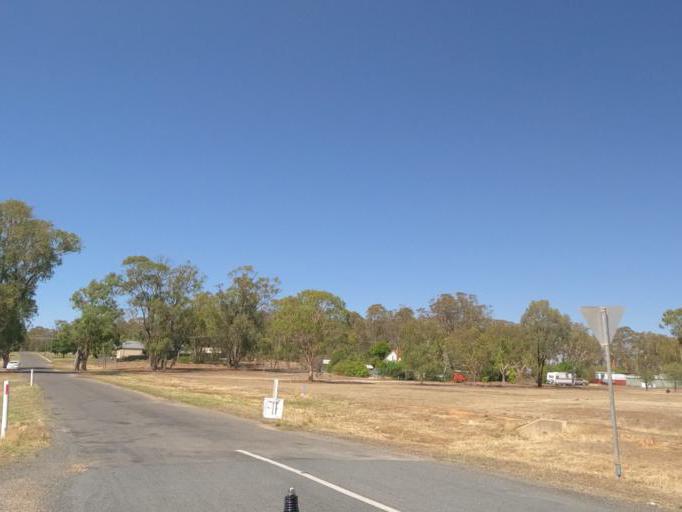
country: AU
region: New South Wales
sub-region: Corowa Shire
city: Mulwala
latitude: -35.9916
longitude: 145.9957
